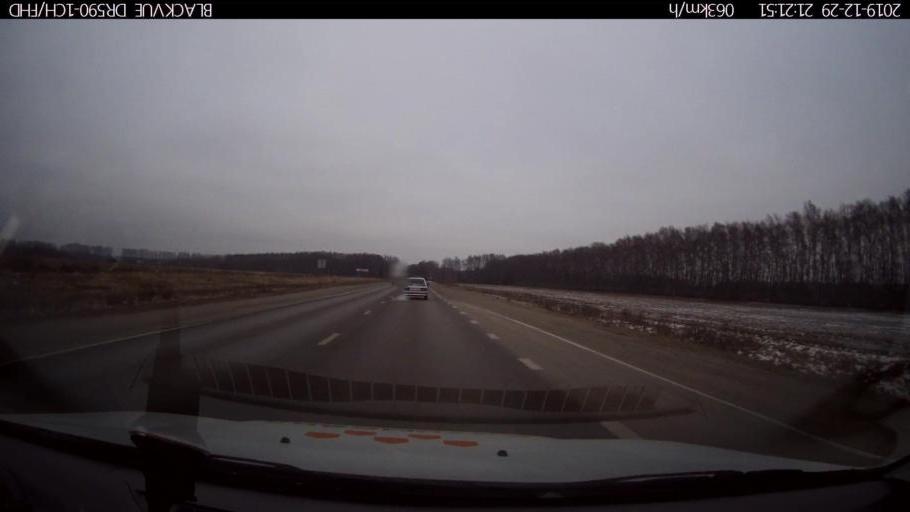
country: RU
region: Nizjnij Novgorod
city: Afonino
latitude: 56.2132
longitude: 44.0275
